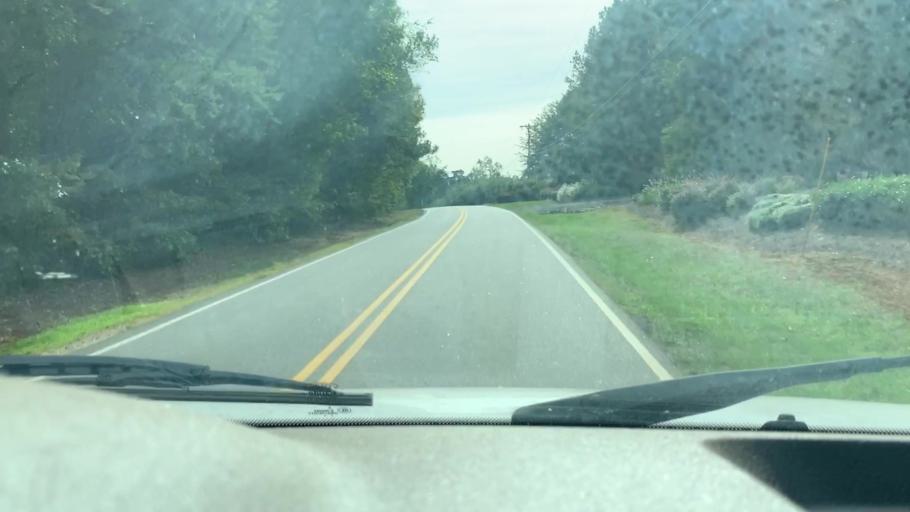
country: US
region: North Carolina
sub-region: Catawba County
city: Lake Norman of Catawba
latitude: 35.5690
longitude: -80.9334
